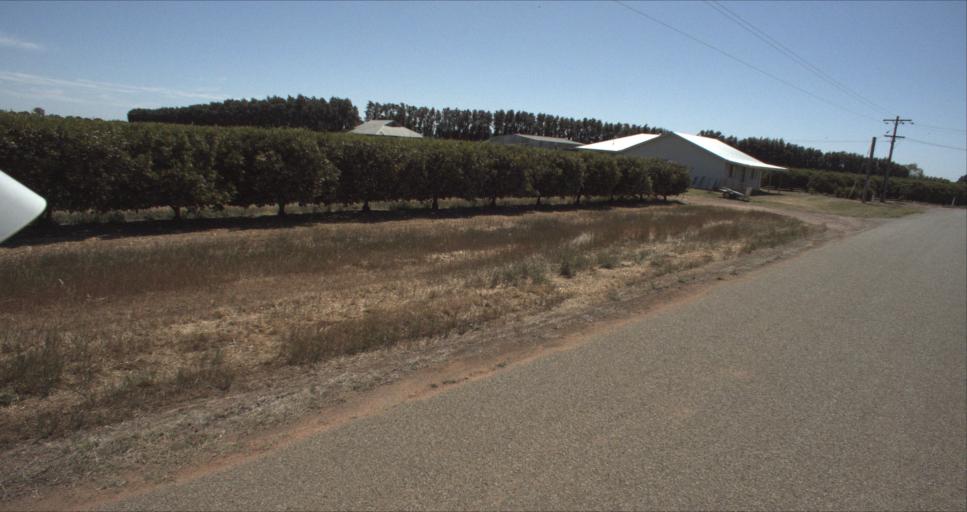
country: AU
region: New South Wales
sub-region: Leeton
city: Leeton
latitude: -34.5394
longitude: 146.3521
